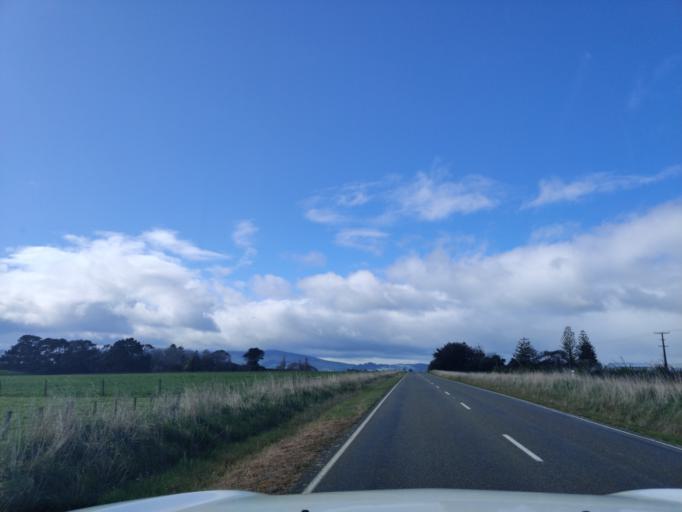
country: NZ
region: Manawatu-Wanganui
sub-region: Palmerston North City
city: Palmerston North
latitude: -40.2879
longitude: 175.6820
